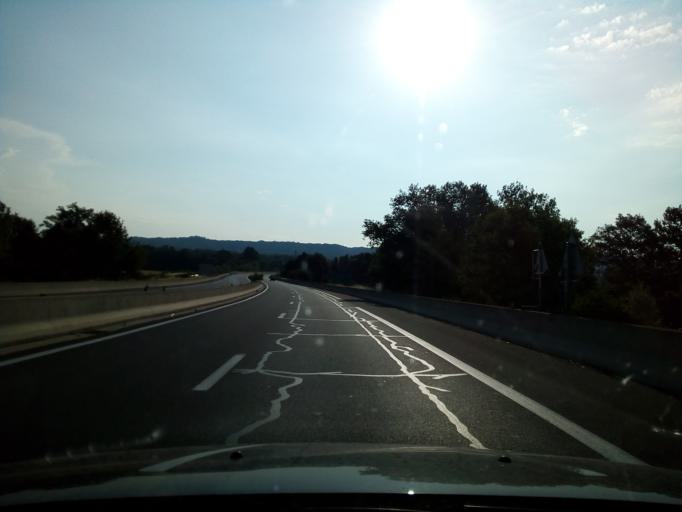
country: FR
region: Auvergne
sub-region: Departement de l'Allier
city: Saint-Victor
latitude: 46.3763
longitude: 2.5962
